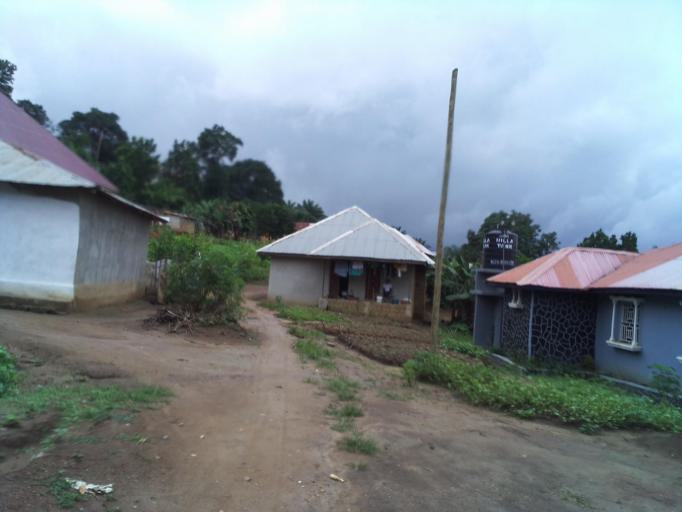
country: SL
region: Eastern Province
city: Kenema
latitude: 7.8786
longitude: -11.1693
